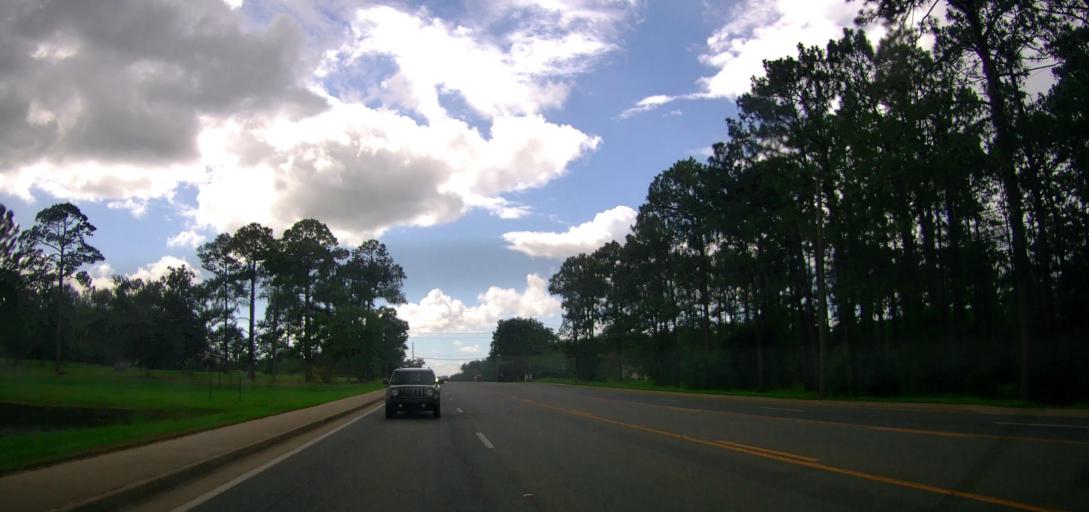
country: US
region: Georgia
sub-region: Coffee County
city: Douglas
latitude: 31.5152
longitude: -82.8779
